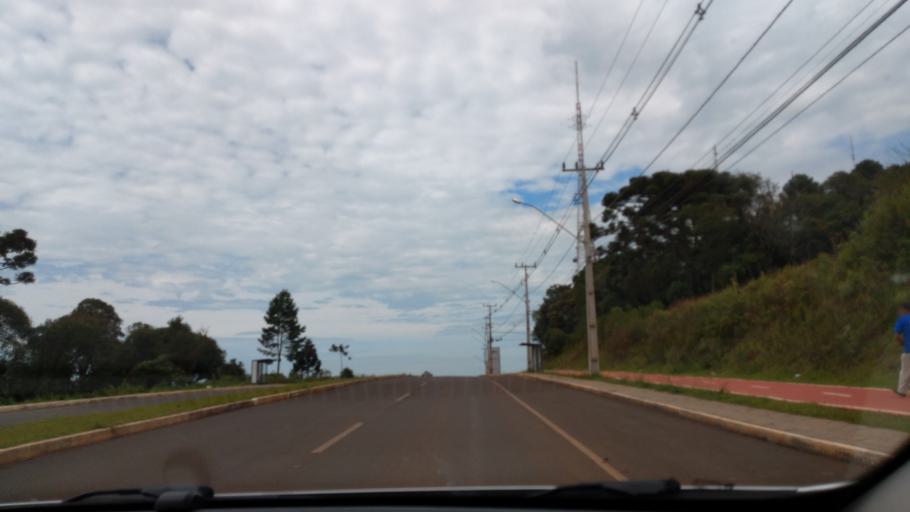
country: BR
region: Parana
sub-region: Guarapuava
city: Guarapuava
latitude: -25.3653
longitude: -51.4338
